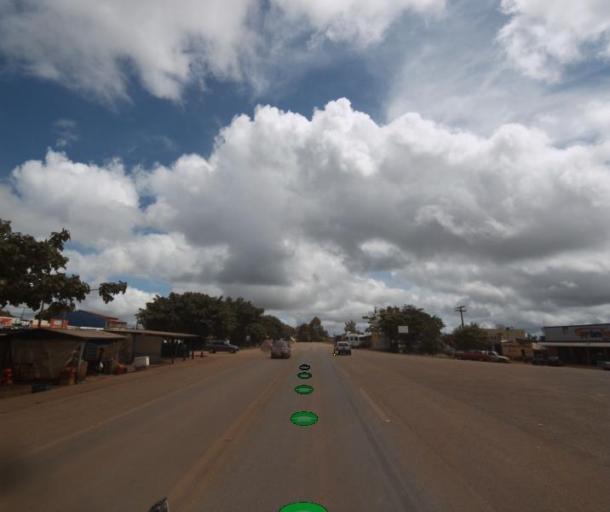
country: BR
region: Federal District
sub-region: Brasilia
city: Brasilia
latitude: -15.7367
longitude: -48.4018
